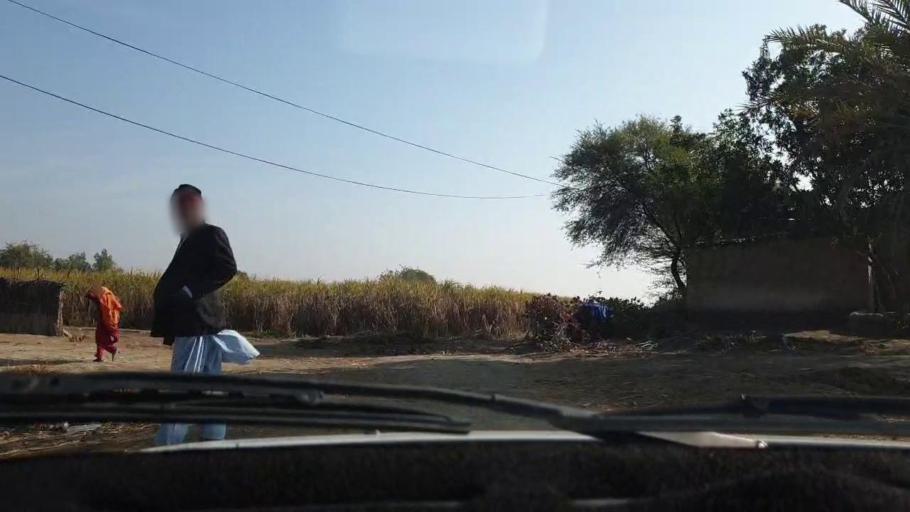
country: PK
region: Sindh
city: Tando Muhammad Khan
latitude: 25.0264
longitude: 68.4887
